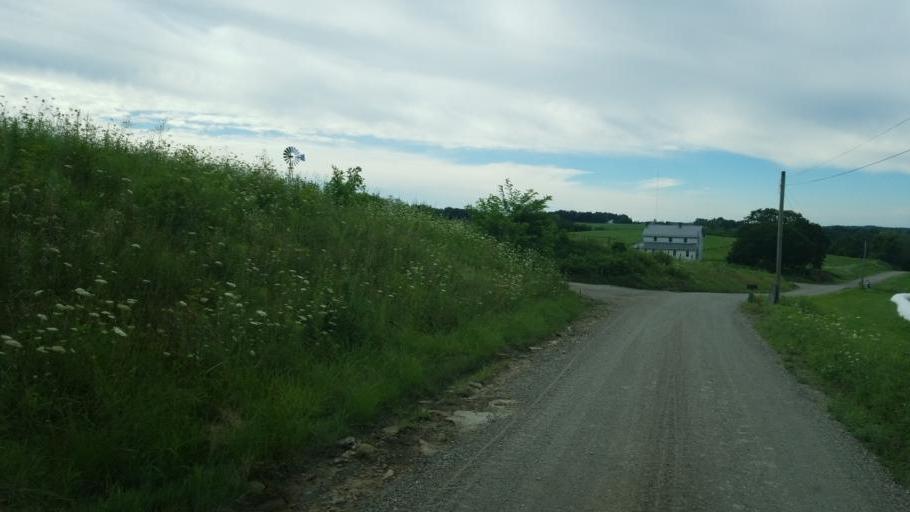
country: US
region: Ohio
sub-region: Holmes County
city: Millersburg
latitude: 40.4975
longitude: -81.8490
